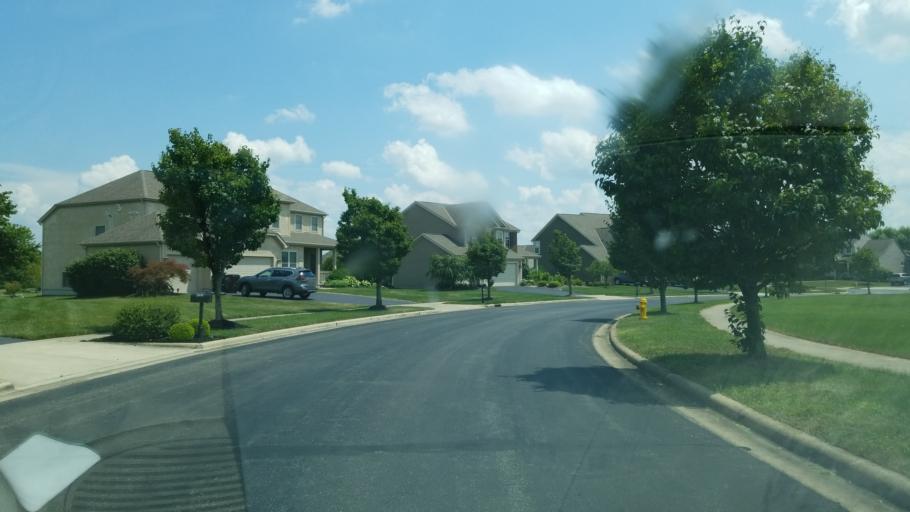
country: US
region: Ohio
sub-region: Delaware County
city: Lewis Center
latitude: 40.2210
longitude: -83.0022
